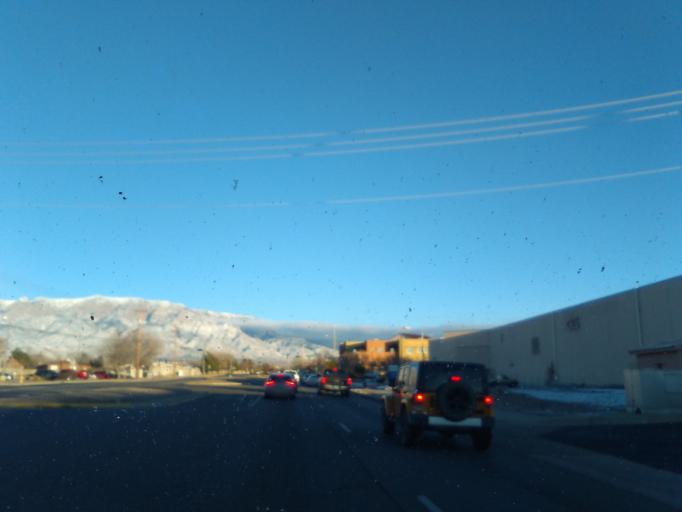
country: US
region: New Mexico
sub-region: Bernalillo County
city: North Valley
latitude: 35.1845
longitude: -106.5936
